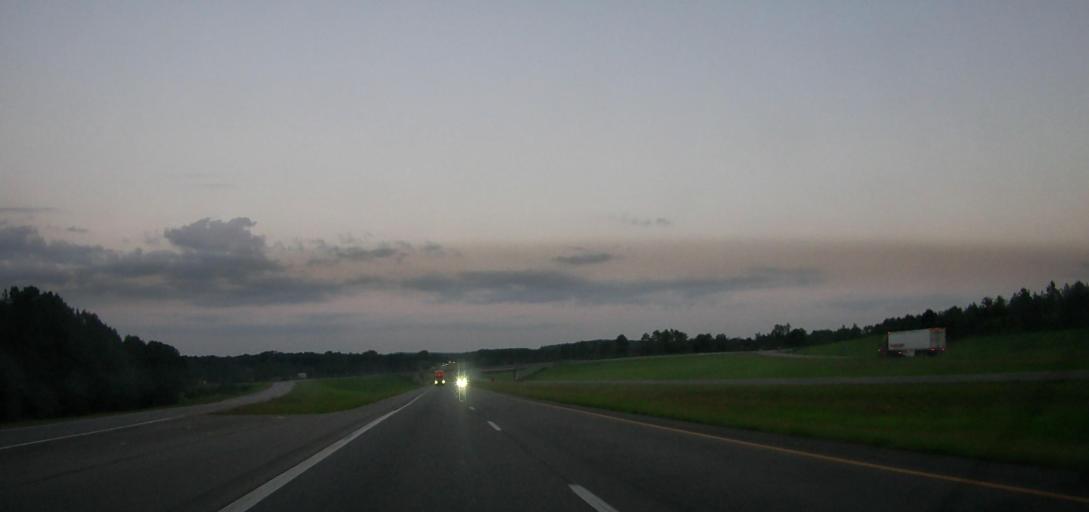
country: US
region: Alabama
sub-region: Marion County
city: Hamilton
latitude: 34.1703
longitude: -88.0660
